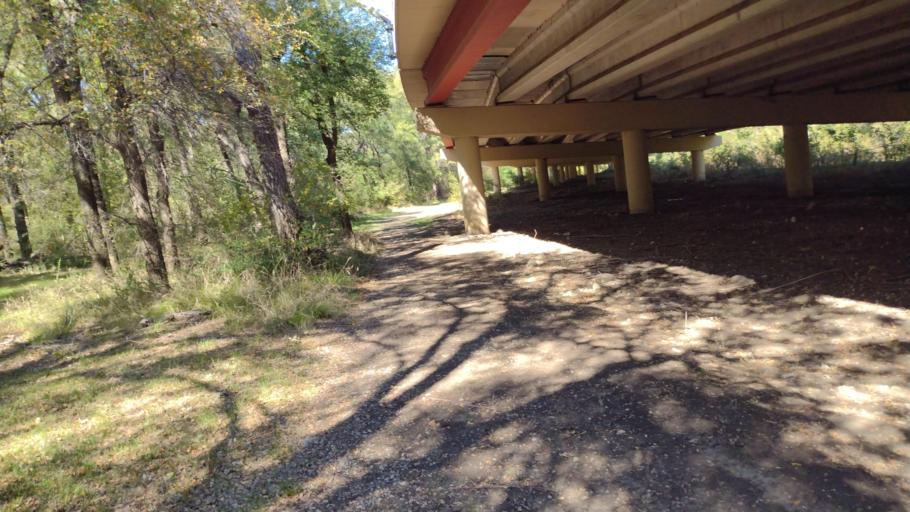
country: US
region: Texas
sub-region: Dallas County
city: Farmers Branch
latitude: 32.9169
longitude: -96.9359
